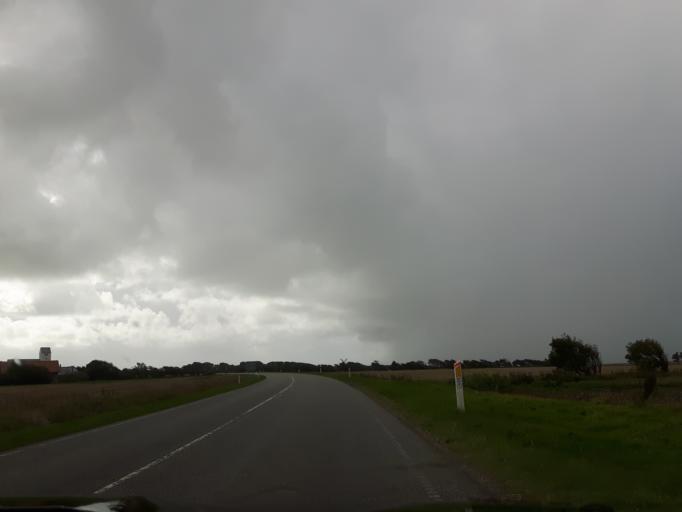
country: DK
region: North Denmark
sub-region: Thisted Kommune
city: Hurup
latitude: 56.7804
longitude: 8.3218
